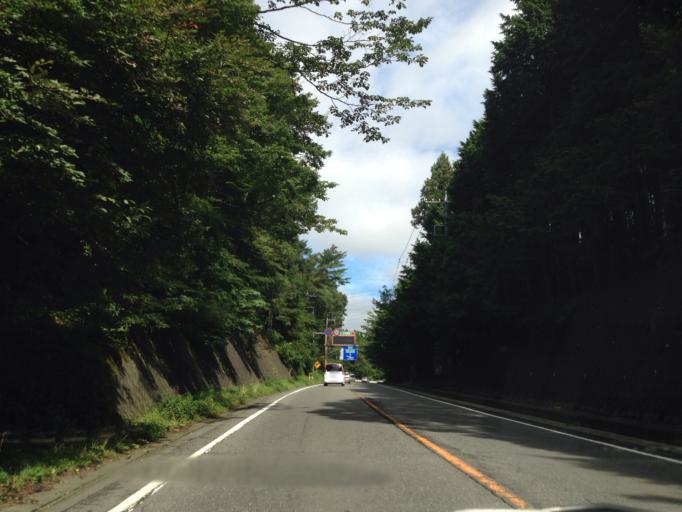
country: JP
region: Shizuoka
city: Gotemba
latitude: 35.3501
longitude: 138.8765
